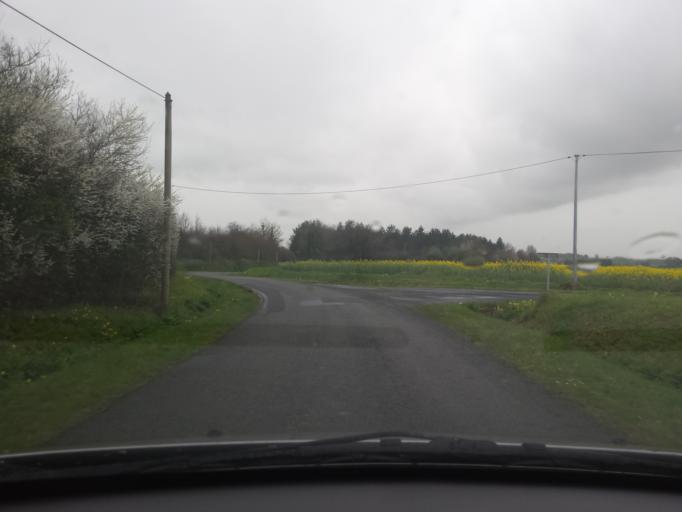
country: FR
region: Pays de la Loire
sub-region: Departement de la Vendee
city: Sainte-Hermine
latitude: 46.5812
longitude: -1.0814
